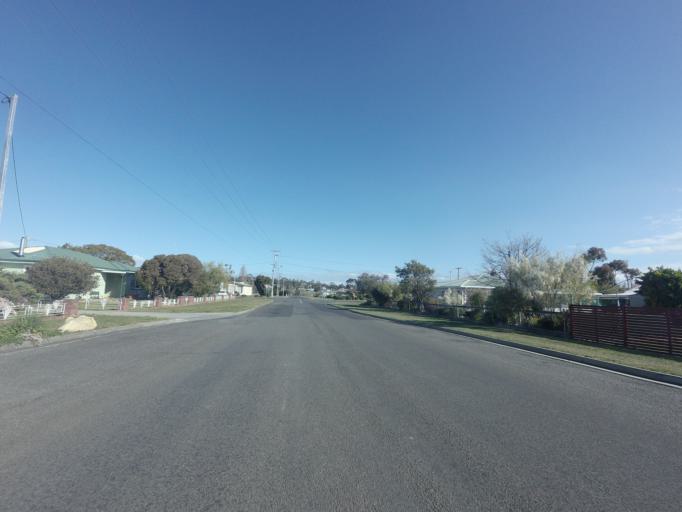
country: AU
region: Tasmania
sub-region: Sorell
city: Sorell
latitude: -42.5071
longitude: 147.9164
